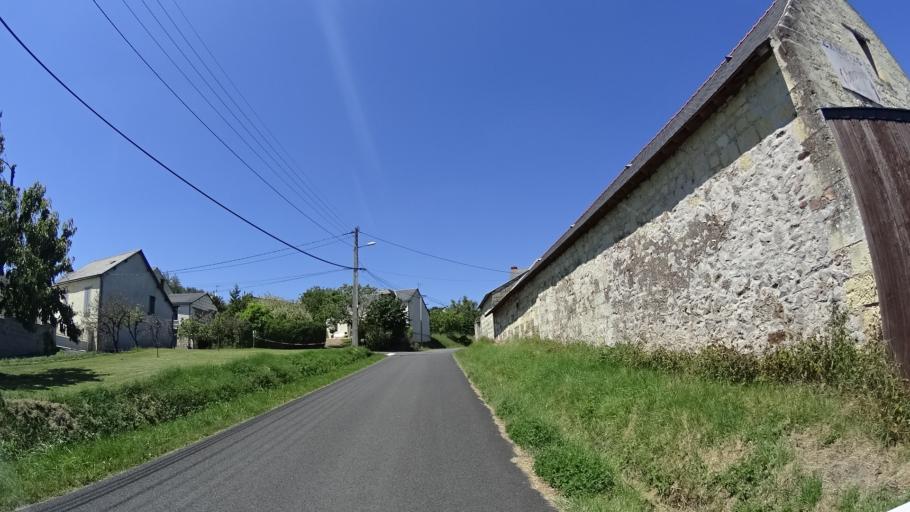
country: FR
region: Pays de la Loire
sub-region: Departement de Maine-et-Loire
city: Saint-Martin-de-la-Place
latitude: 47.2821
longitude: -0.1332
